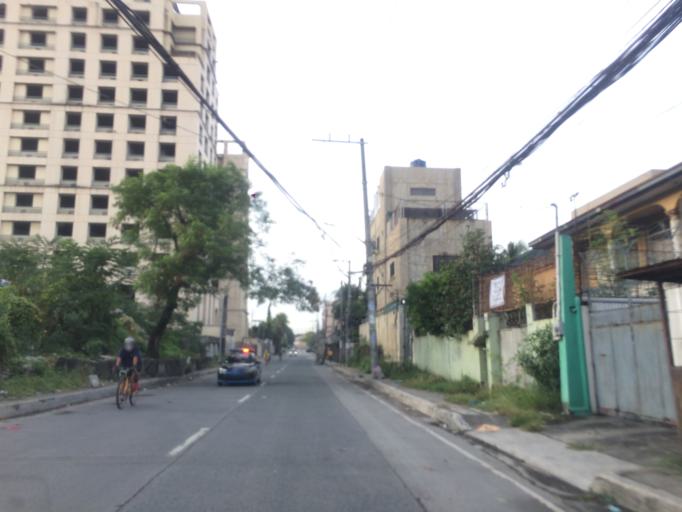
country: PH
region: Calabarzon
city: Del Monte
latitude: 14.6324
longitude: 121.0048
